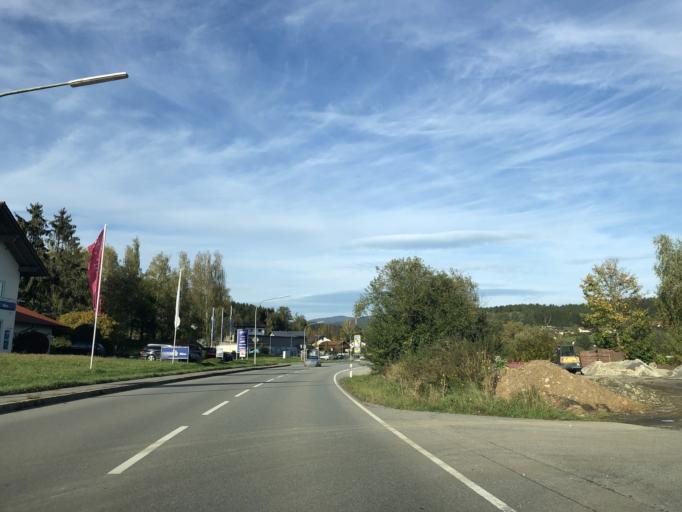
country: DE
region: Bavaria
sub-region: Lower Bavaria
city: Teisnach
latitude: 49.0316
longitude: 12.9911
